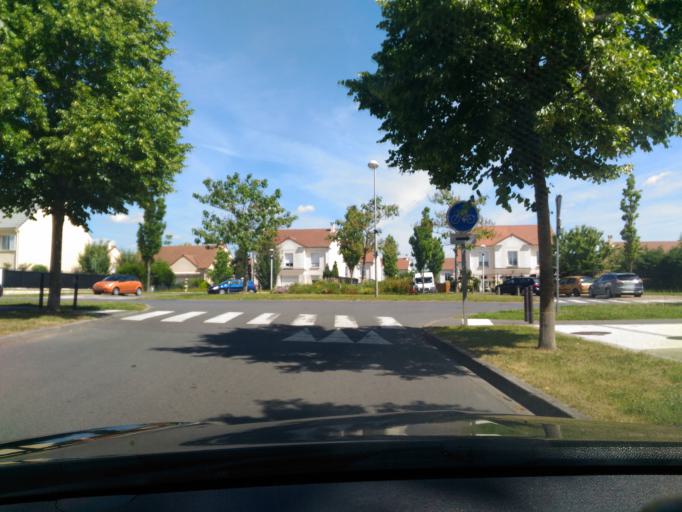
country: FR
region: Ile-de-France
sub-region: Departement de Seine-et-Marne
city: Moissy-Cramayel
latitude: 48.6317
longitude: 2.5804
